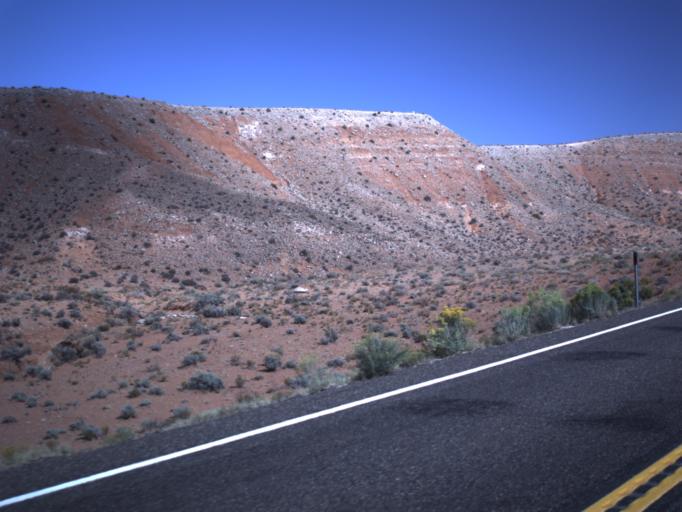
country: US
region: Utah
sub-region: Wayne County
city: Loa
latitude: 38.1454
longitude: -110.6141
